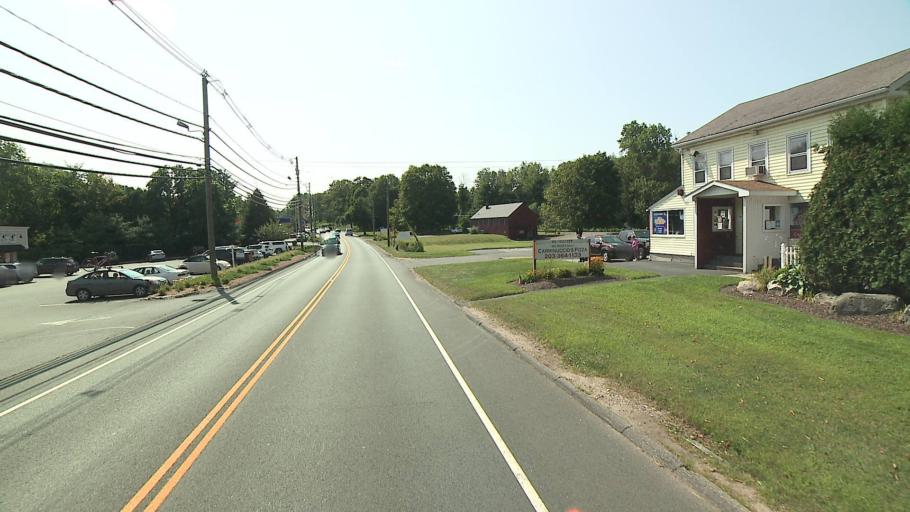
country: US
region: Connecticut
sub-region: Fairfield County
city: Newtown
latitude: 41.3975
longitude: -73.2944
